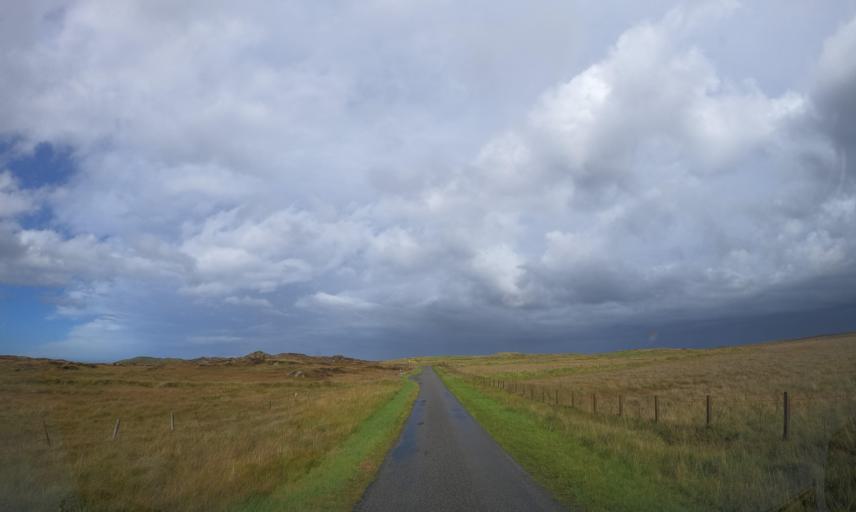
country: GB
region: Scotland
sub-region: Eilean Siar
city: Barra
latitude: 56.5204
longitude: -6.8407
